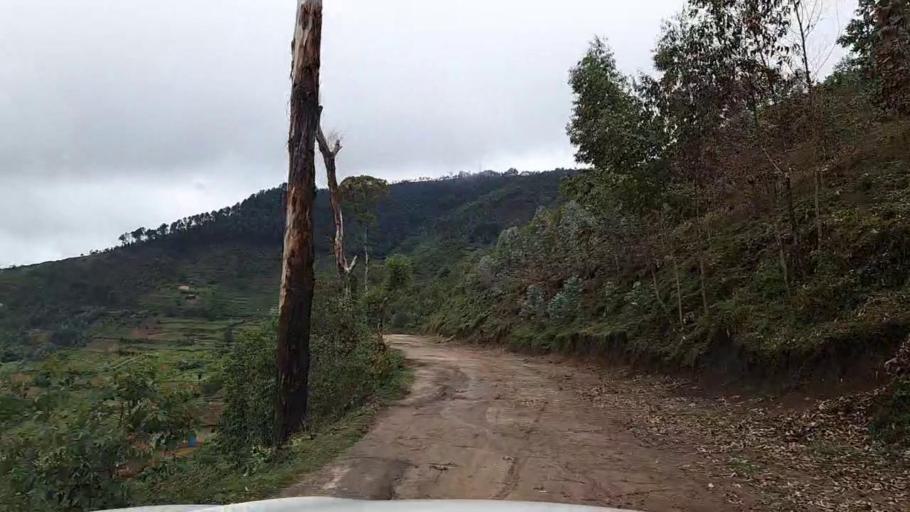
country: RW
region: Southern Province
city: Gikongoro
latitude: -2.3642
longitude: 29.4953
